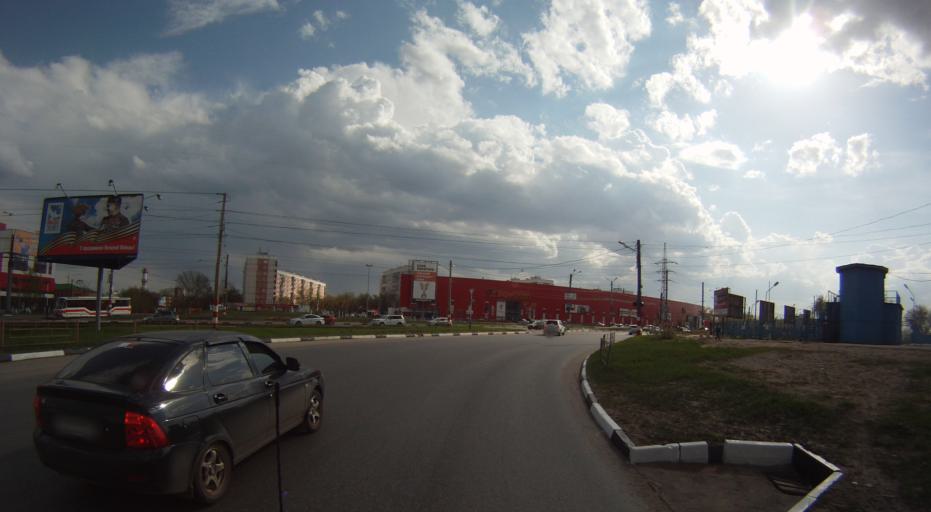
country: RU
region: Nizjnij Novgorod
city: Nizhniy Novgorod
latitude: 56.2978
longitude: 43.9428
